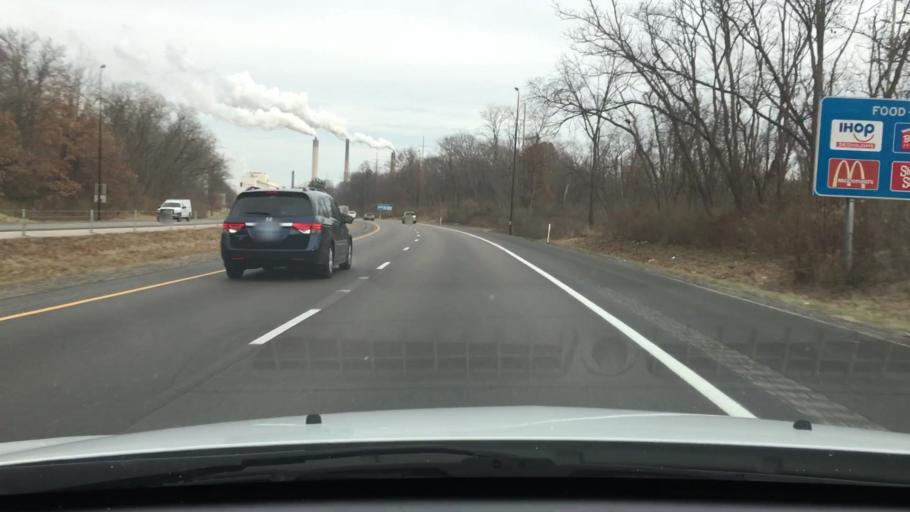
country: US
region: Illinois
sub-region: Sangamon County
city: Southern View
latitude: 39.7460
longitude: -89.6239
